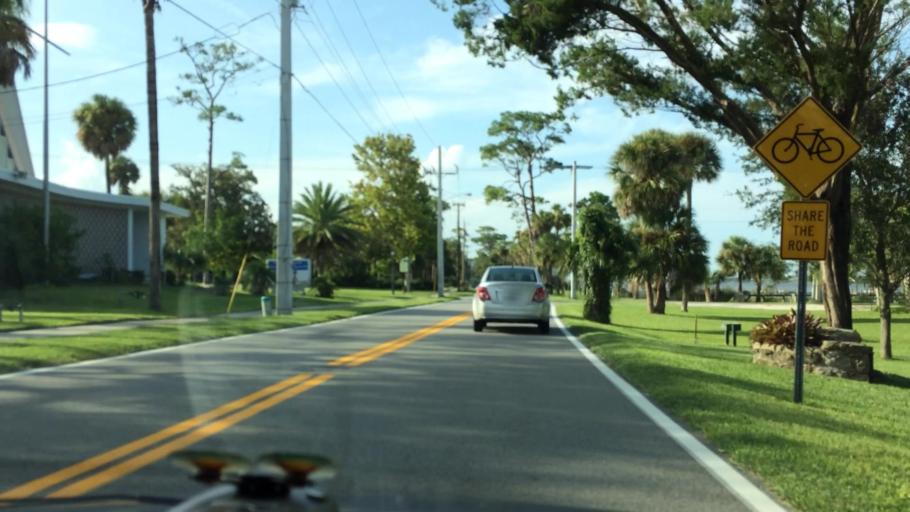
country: US
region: Florida
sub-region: Volusia County
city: Ormond Beach
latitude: 29.2870
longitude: -81.0561
